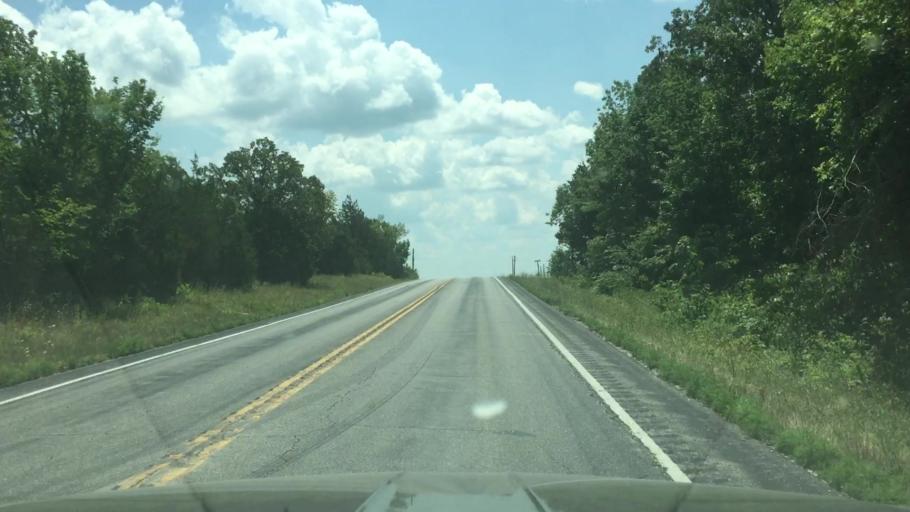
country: US
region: Missouri
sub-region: Miller County
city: Tuscumbia
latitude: 38.1149
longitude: -92.5081
